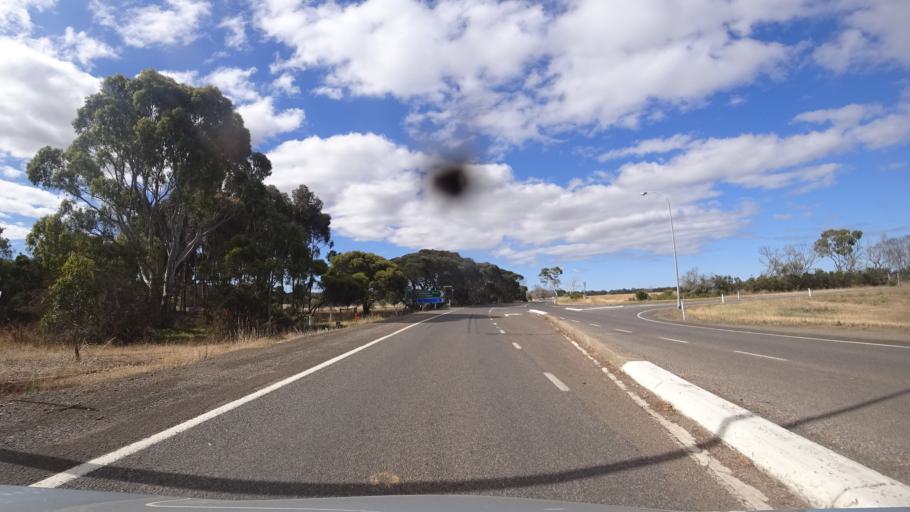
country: AU
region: South Australia
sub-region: Kangaroo Island
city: Kingscote
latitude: -35.7076
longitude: 137.5133
